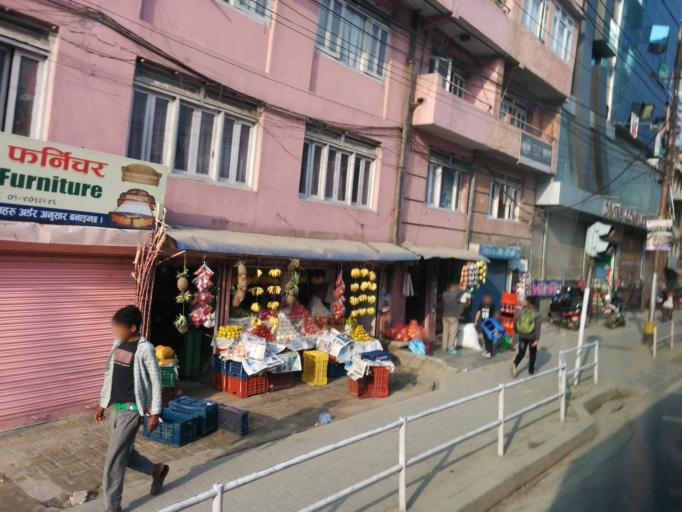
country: NP
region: Central Region
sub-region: Bagmati Zone
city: Kathmandu
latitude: 27.6984
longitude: 85.3009
